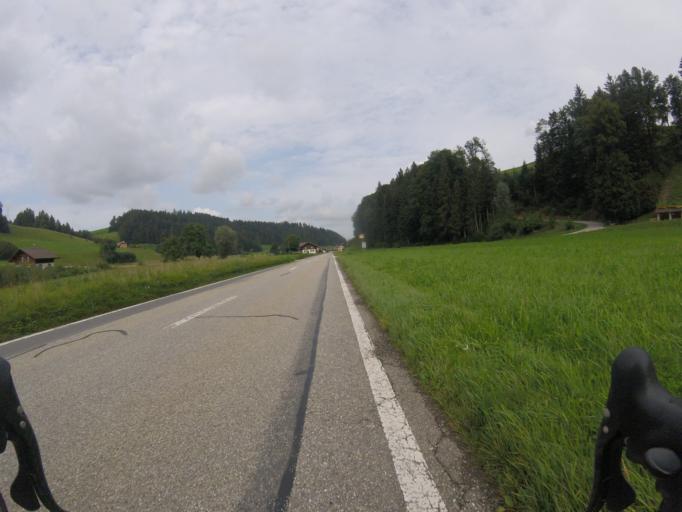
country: CH
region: Bern
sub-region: Emmental District
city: Lutzelfluh
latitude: 46.9918
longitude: 7.6882
